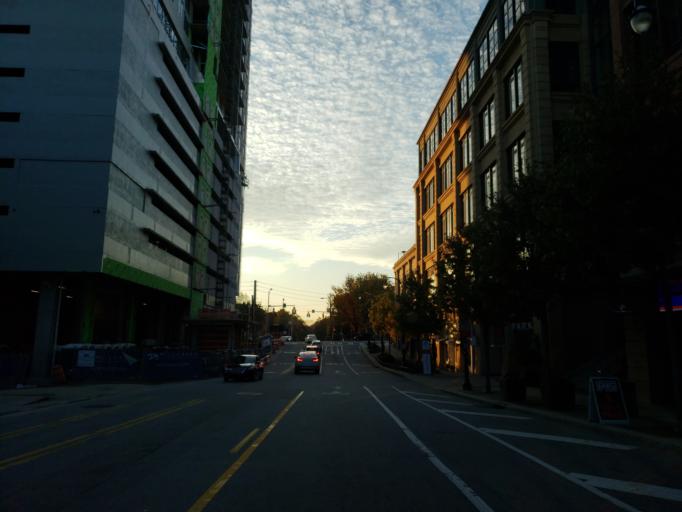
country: US
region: Georgia
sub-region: DeKalb County
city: North Atlanta
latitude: 33.8371
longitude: -84.3799
